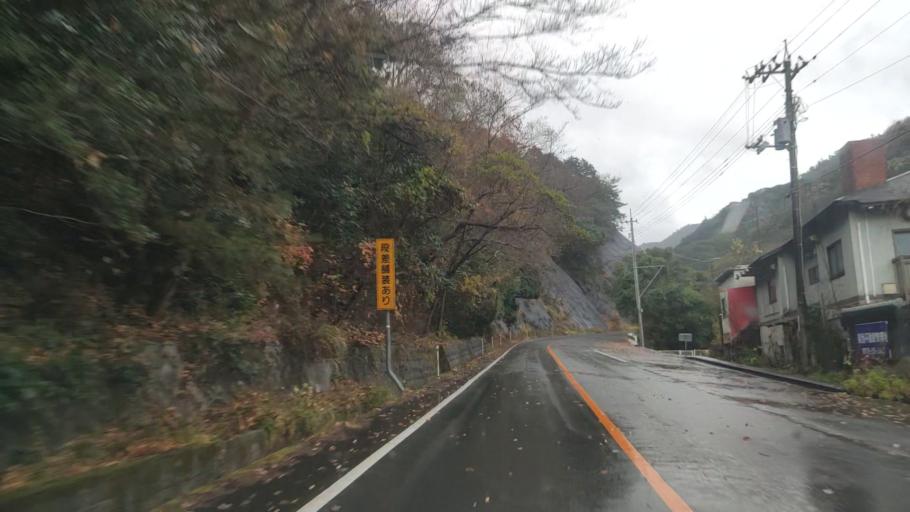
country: JP
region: Tokushima
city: Kamojimacho-jogejima
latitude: 34.1902
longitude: 134.3360
